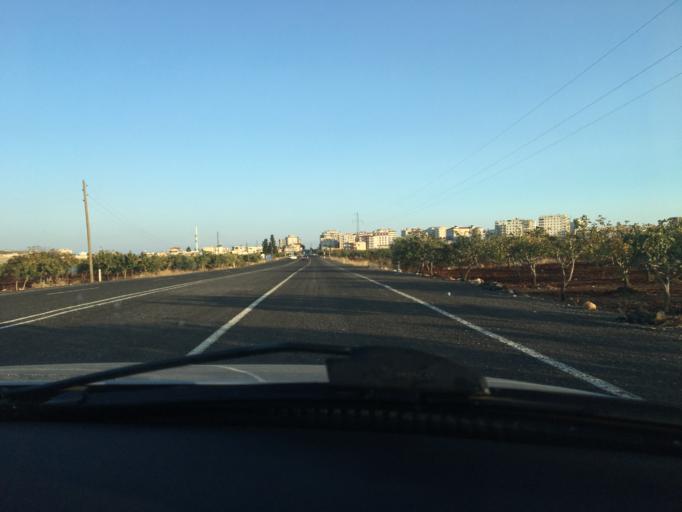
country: TR
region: Sanliurfa
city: Halfeti
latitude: 37.2340
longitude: 37.9350
